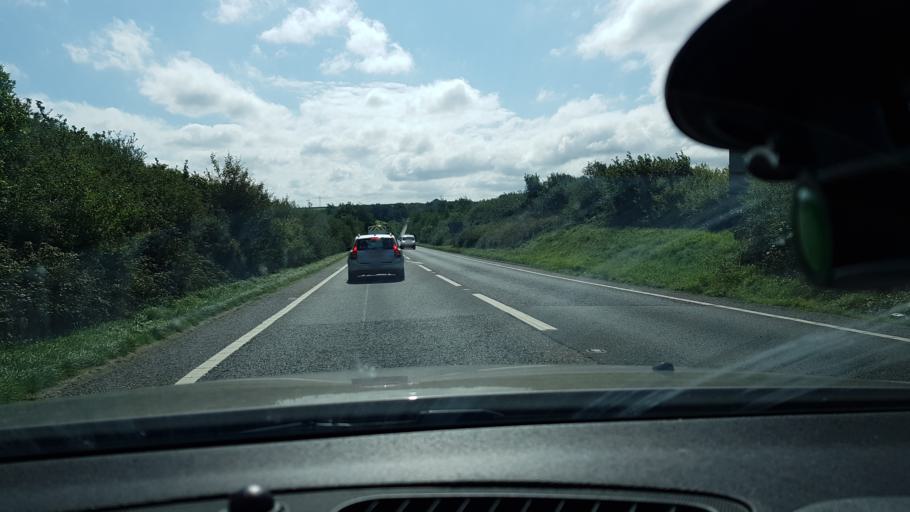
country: GB
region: England
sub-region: Cornwall
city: Truro
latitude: 50.3277
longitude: -5.0728
